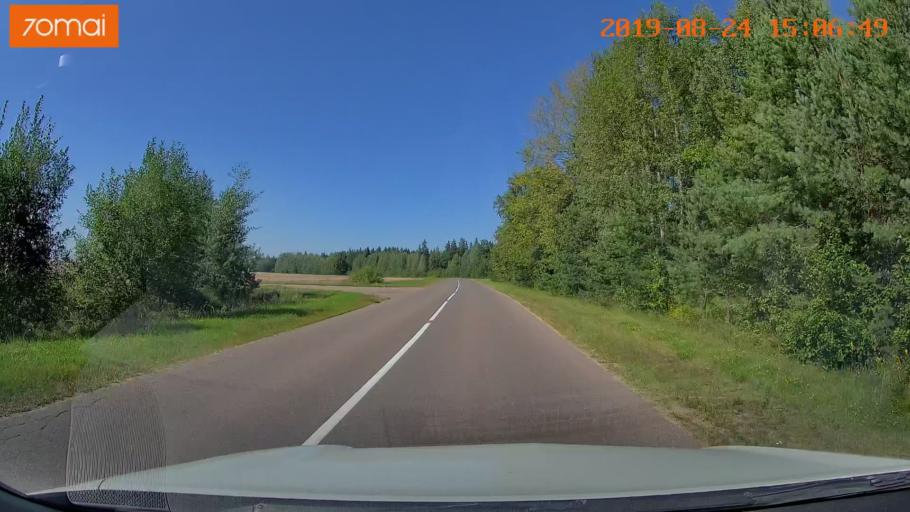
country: BY
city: Michanovichi
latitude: 53.6038
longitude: 27.6791
